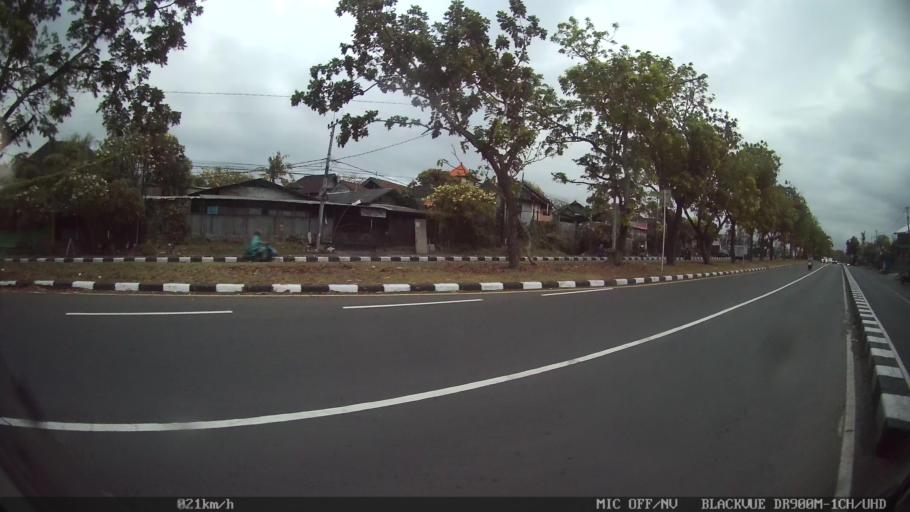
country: ID
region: Bali
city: Banjar Pasekan
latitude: -8.6437
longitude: 115.2782
